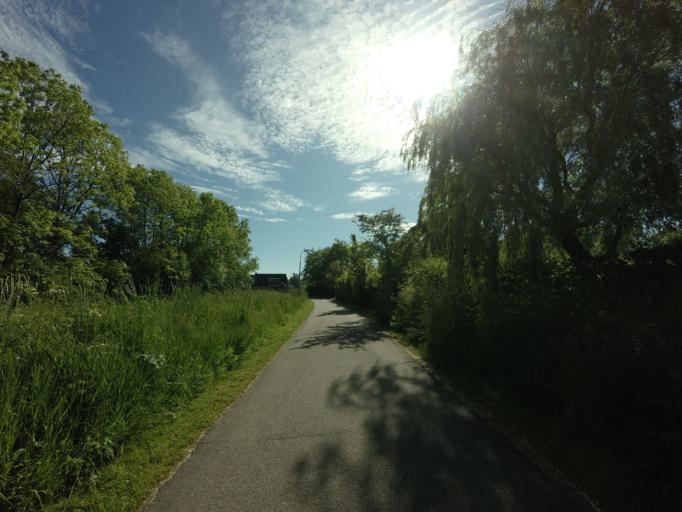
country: NL
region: North Holland
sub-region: Gemeente Uitgeest
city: Uitgeest
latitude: 52.5067
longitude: 4.7478
